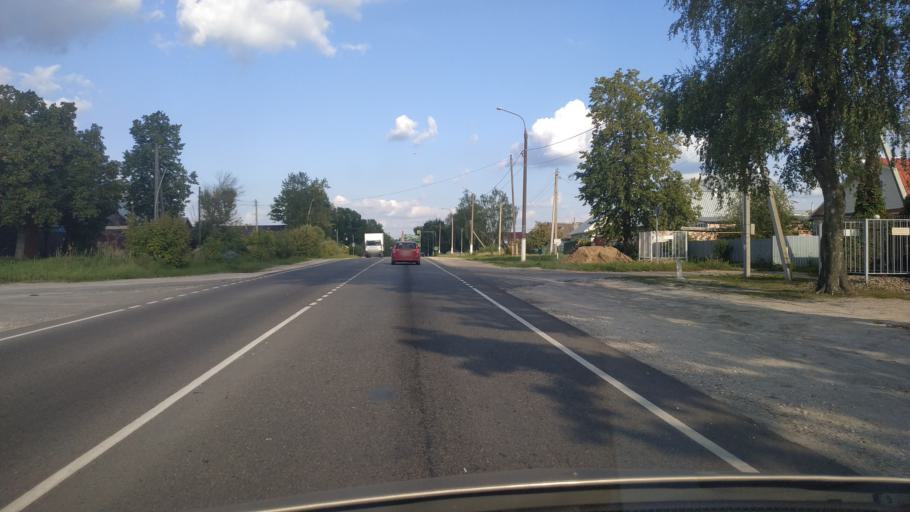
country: RU
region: Moskovskaya
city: Shaturtorf
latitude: 55.5794
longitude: 39.4748
